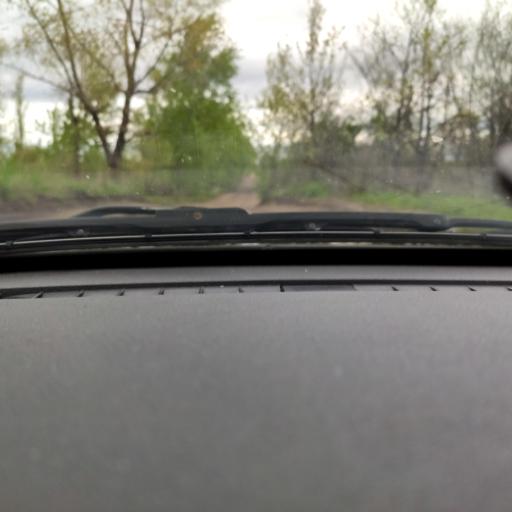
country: RU
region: Voronezj
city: Maslovka
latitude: 51.4970
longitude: 39.2100
